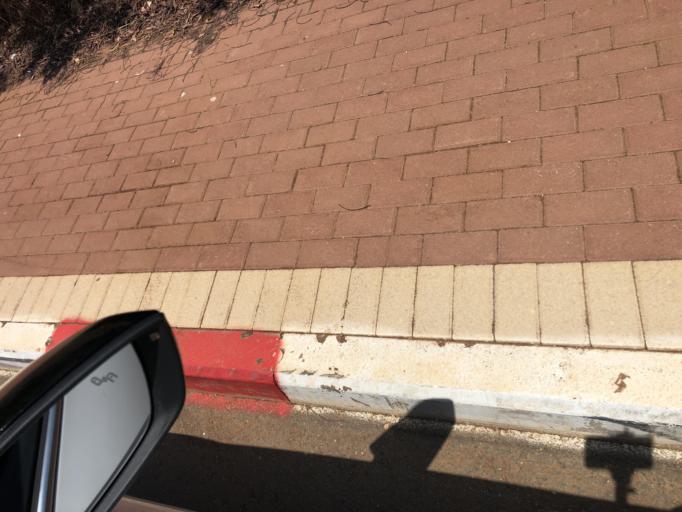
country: IL
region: Haifa
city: Daliyat el Karmil
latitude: 32.6494
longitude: 35.0997
